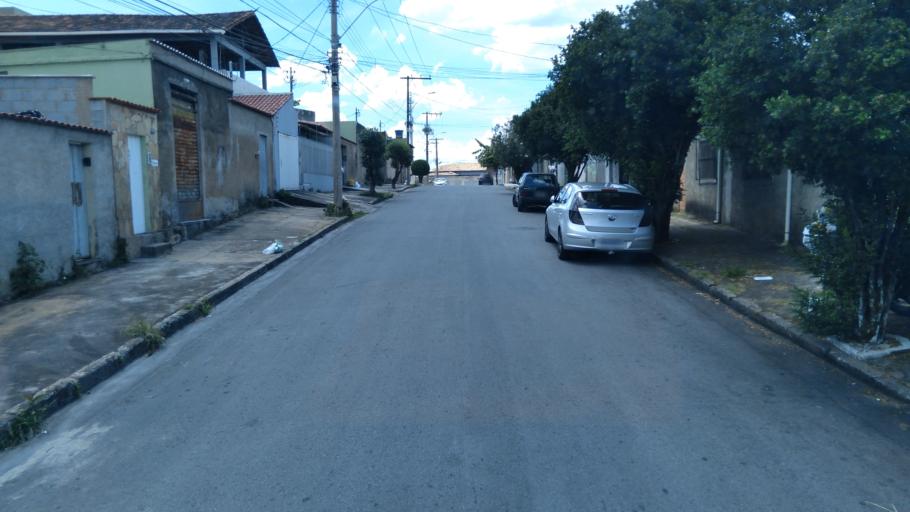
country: BR
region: Minas Gerais
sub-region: Contagem
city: Contagem
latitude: -19.8922
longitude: -44.0135
